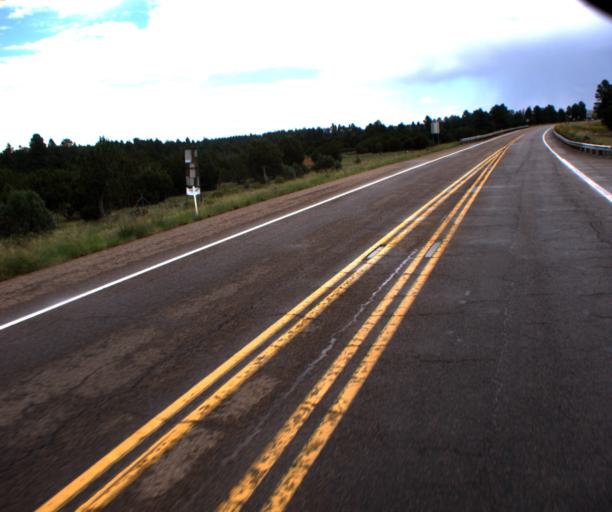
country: US
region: Arizona
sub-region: Navajo County
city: Heber-Overgaard
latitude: 34.3933
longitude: -110.5241
